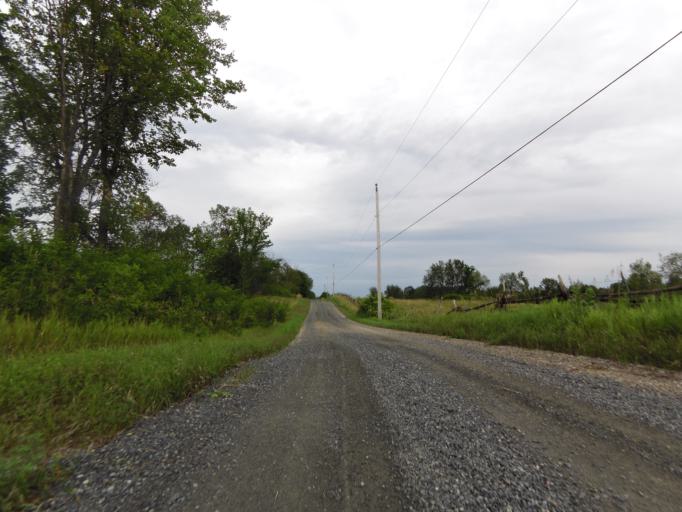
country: CA
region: Ontario
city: Perth
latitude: 45.0586
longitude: -76.3941
